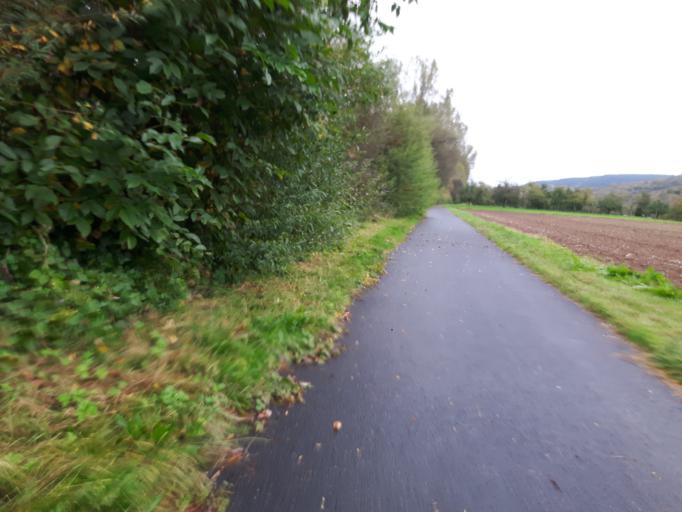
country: DE
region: Bavaria
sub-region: Regierungsbezirk Unterfranken
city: Thungersheim
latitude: 49.8750
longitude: 9.8376
